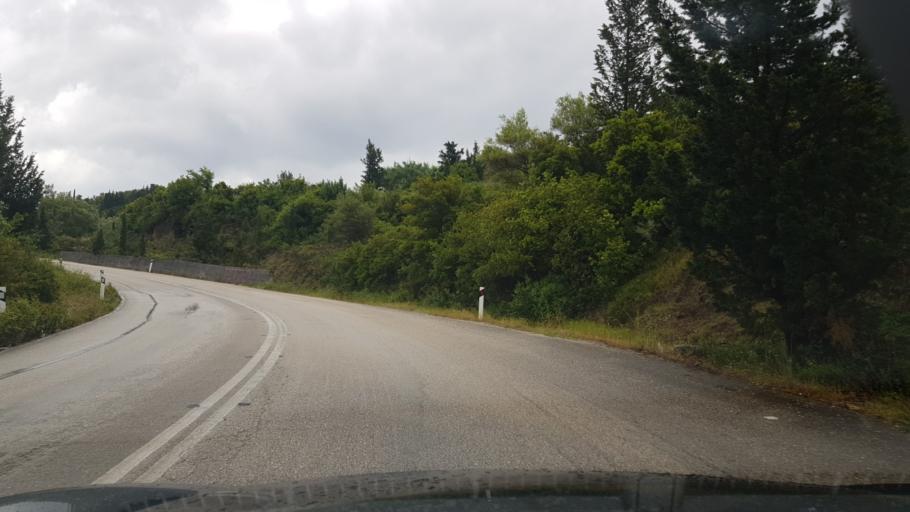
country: GR
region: Ionian Islands
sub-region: Lefkada
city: Nidri
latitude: 38.6345
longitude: 20.6277
